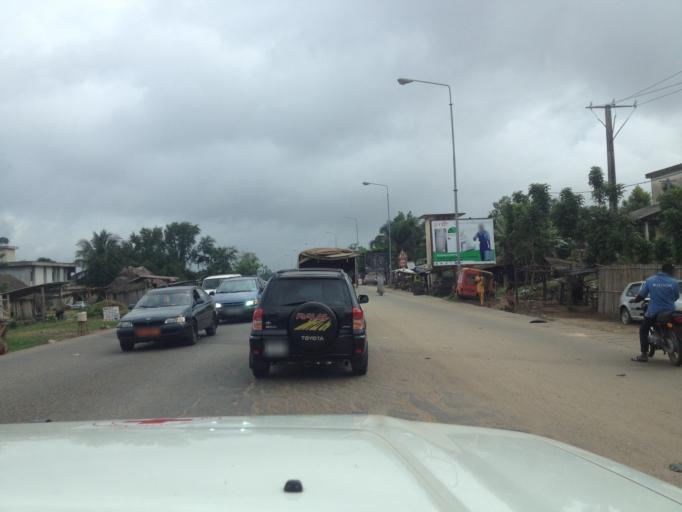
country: BJ
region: Queme
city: Porto-Novo
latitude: 6.4552
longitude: 2.6208
